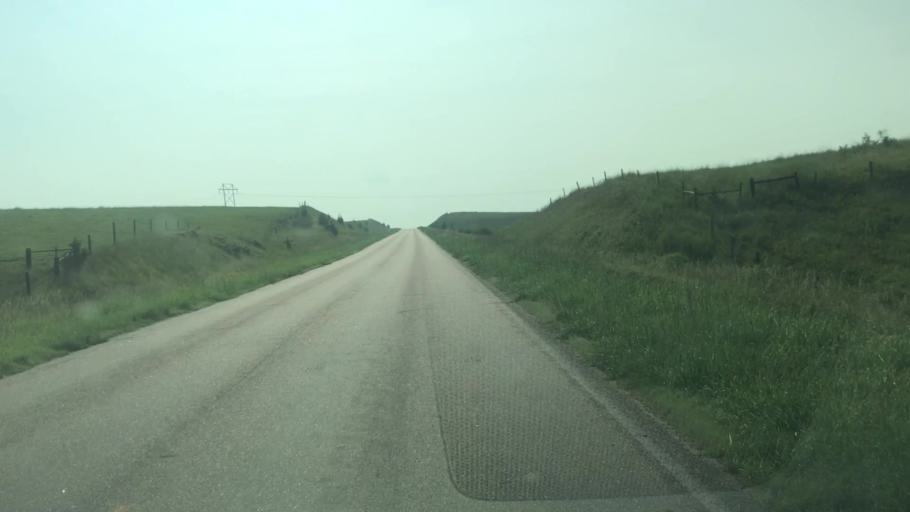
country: US
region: Nebraska
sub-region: Sherman County
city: Loup City
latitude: 41.2793
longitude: -98.9376
